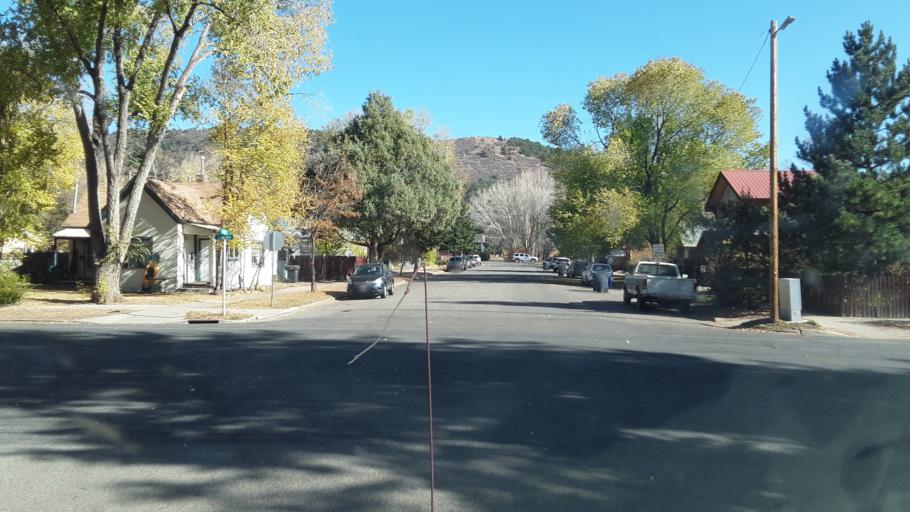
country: US
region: Colorado
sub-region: La Plata County
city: Durango
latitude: 37.2680
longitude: -107.8768
